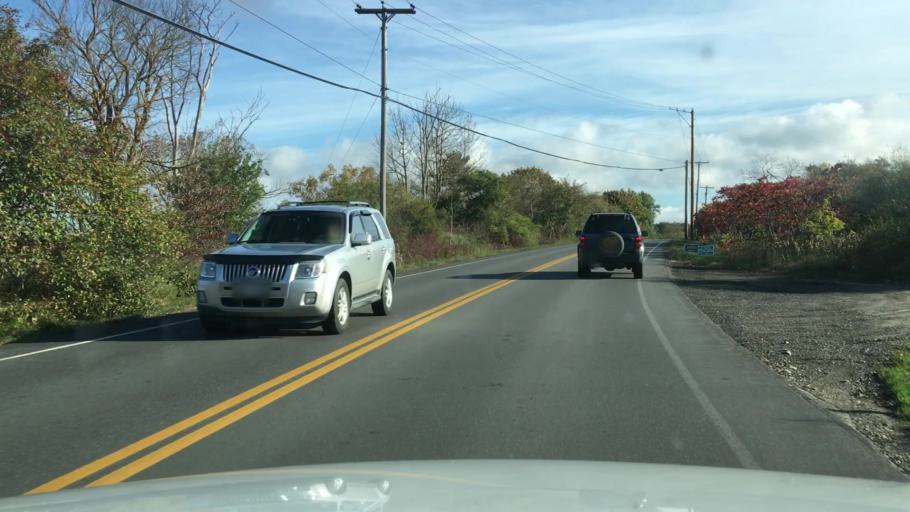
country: US
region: Maine
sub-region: Knox County
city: Thomaston
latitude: 44.0973
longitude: -69.1509
